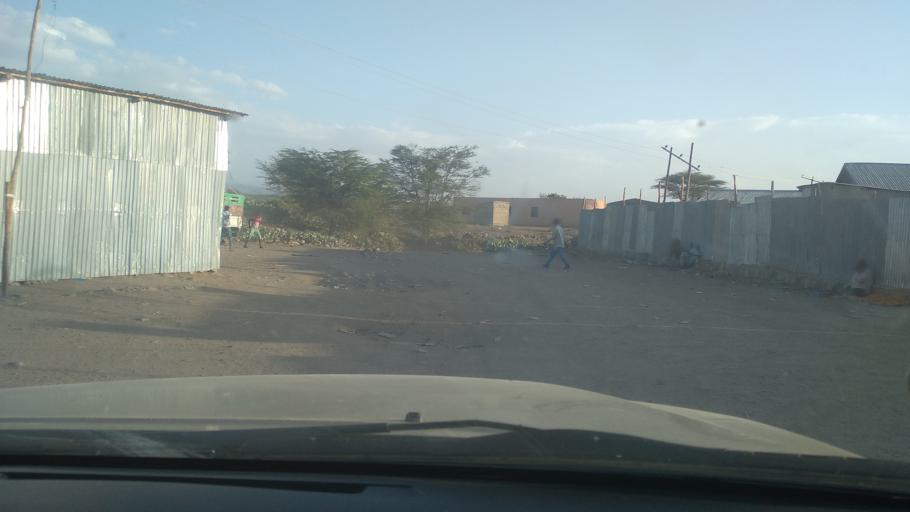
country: ET
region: Oromiya
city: Asbe Teferi
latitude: 9.2915
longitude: 40.8336
